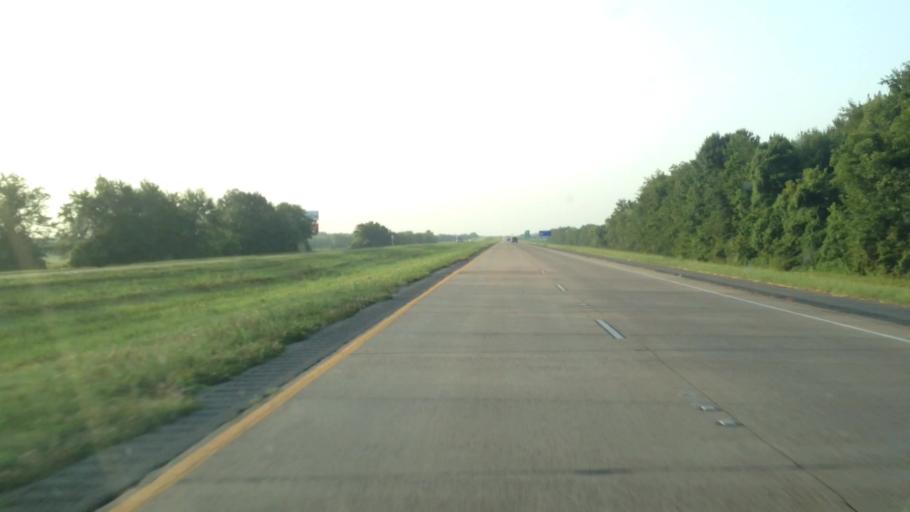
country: US
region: Louisiana
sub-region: Natchitoches Parish
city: Vienna Bend
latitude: 31.6196
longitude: -93.0595
